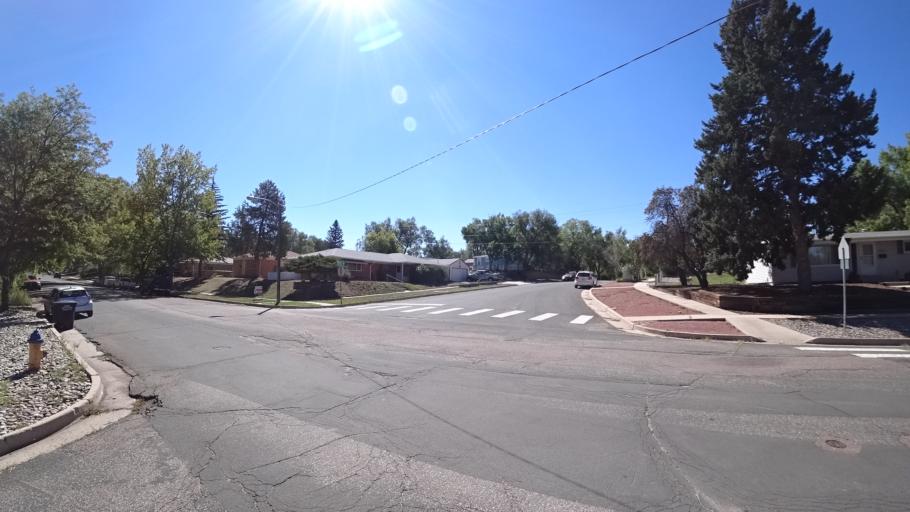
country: US
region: Colorado
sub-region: El Paso County
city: Colorado Springs
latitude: 38.8526
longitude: -104.8060
